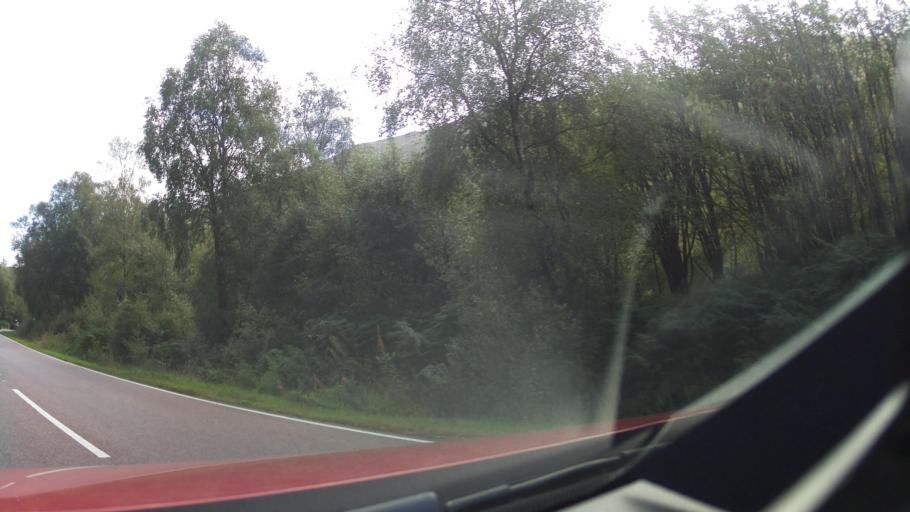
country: GB
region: Scotland
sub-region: Stirling
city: Callander
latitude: 56.4080
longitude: -4.5502
